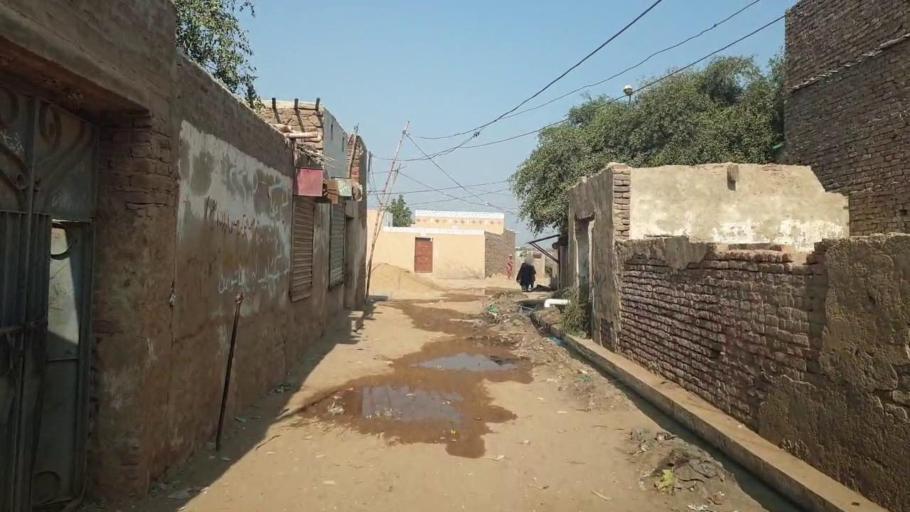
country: PK
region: Sindh
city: Jamshoro
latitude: 25.4384
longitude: 68.2810
